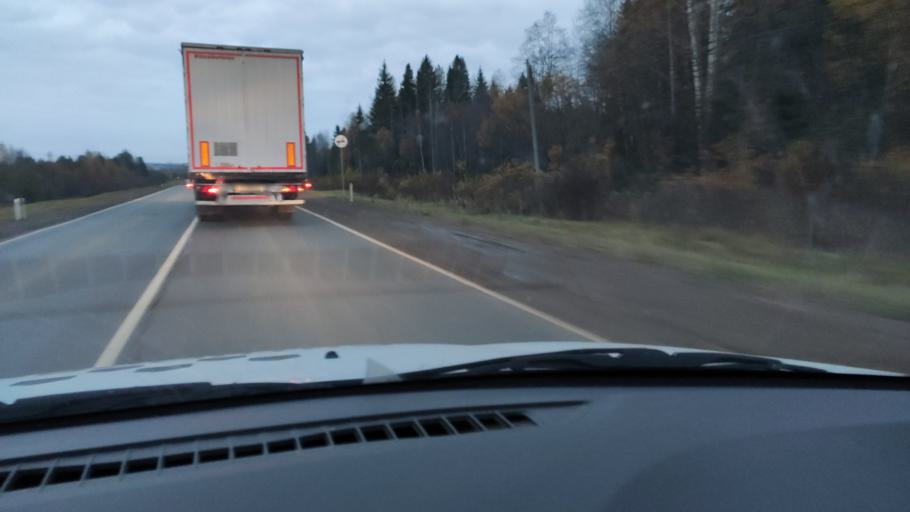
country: RU
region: Kirov
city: Kostino
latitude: 58.8552
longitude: 53.1989
